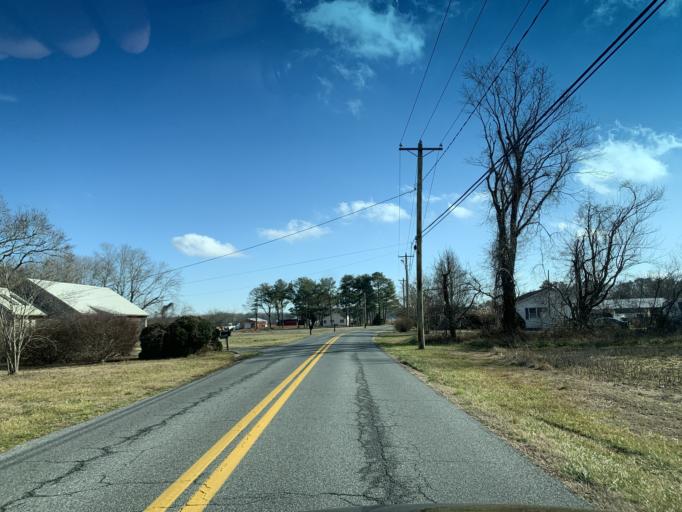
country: US
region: Delaware
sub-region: Sussex County
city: Selbyville
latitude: 38.4532
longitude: -75.1985
